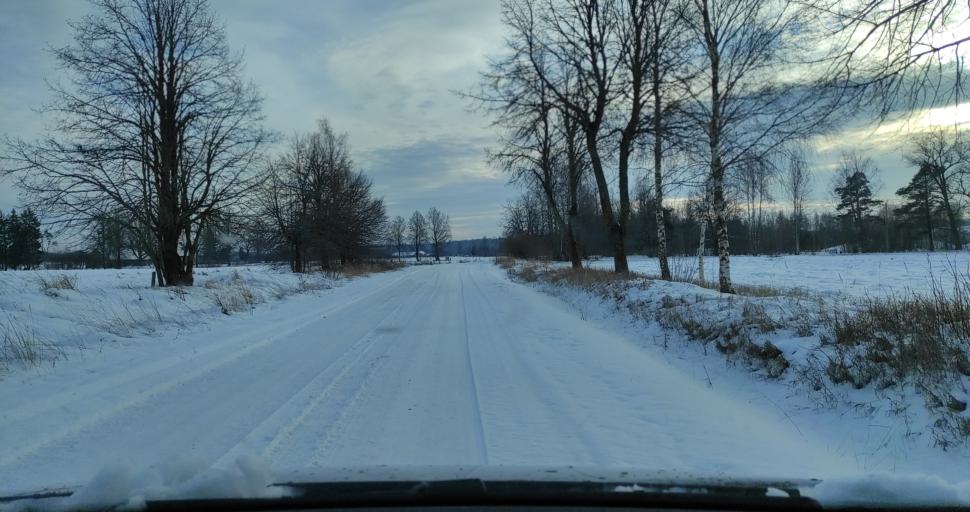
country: LV
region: Kuldigas Rajons
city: Kuldiga
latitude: 56.9432
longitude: 22.0275
